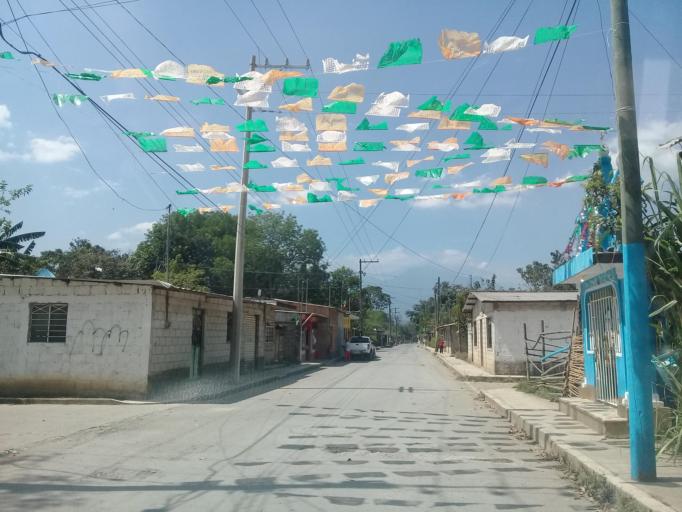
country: MX
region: Veracruz
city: Jalapilla
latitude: 18.8118
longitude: -97.0672
